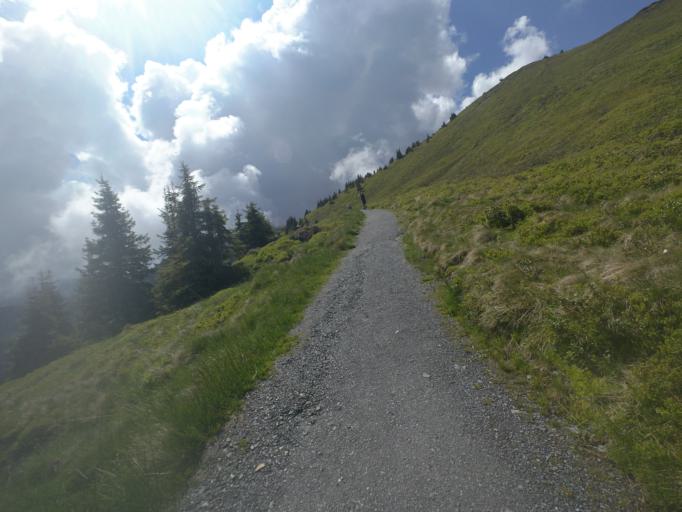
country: AT
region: Salzburg
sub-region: Politischer Bezirk Zell am See
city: Viehhofen
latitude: 47.3989
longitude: 12.7072
